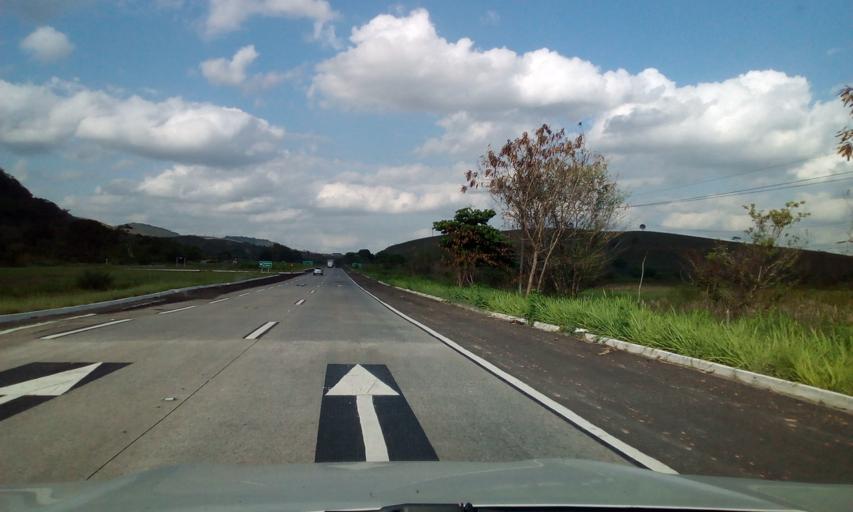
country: BR
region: Pernambuco
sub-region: Joaquim Nabuco
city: Joaquim Nabuco
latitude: -8.6003
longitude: -35.5302
